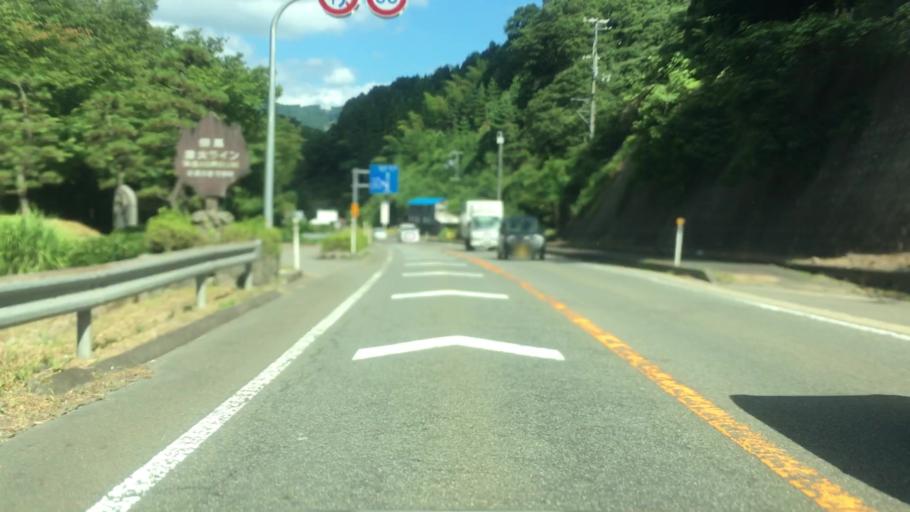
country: JP
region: Hyogo
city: Toyooka
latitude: 35.5838
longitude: 134.7408
